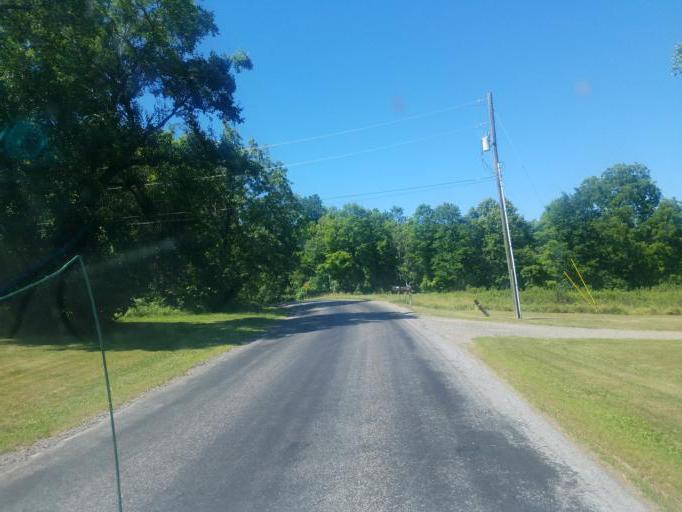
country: US
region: New York
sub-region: Ontario County
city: Naples
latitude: 42.7230
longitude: -77.3073
